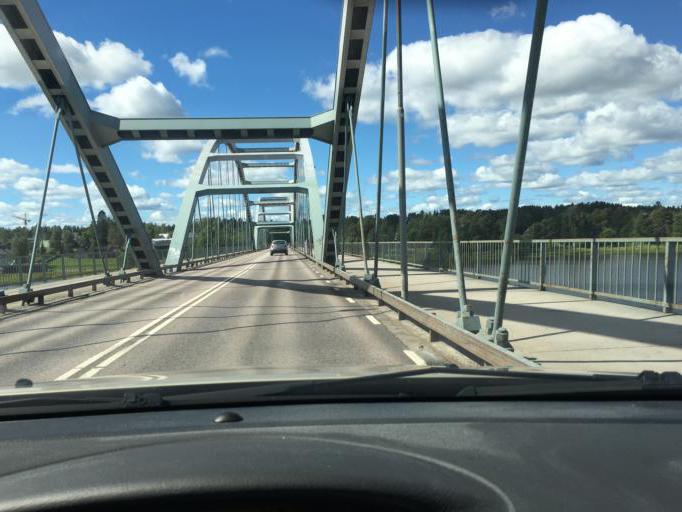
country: SE
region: Norrbotten
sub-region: Lulea Kommun
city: Bergnaset
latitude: 65.5788
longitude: 22.1202
